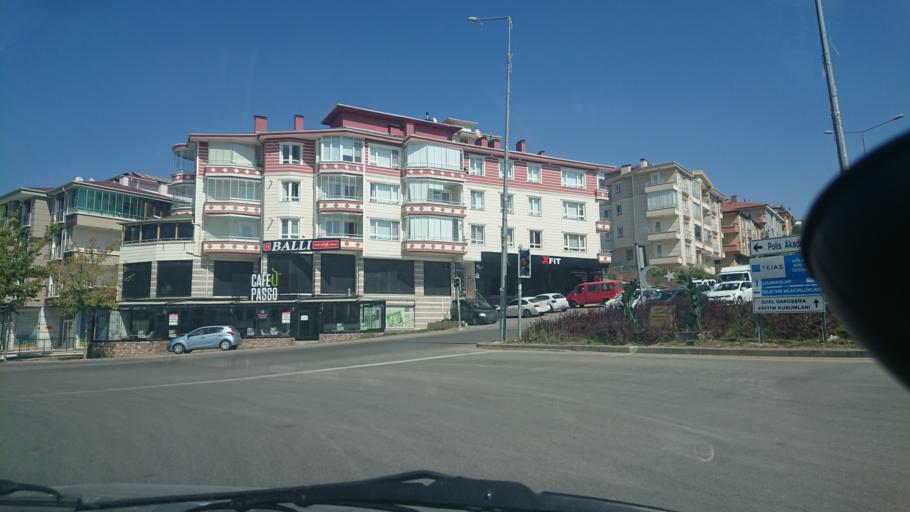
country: TR
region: Ankara
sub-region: Goelbasi
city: Golbasi
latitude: 39.7998
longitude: 32.8122
